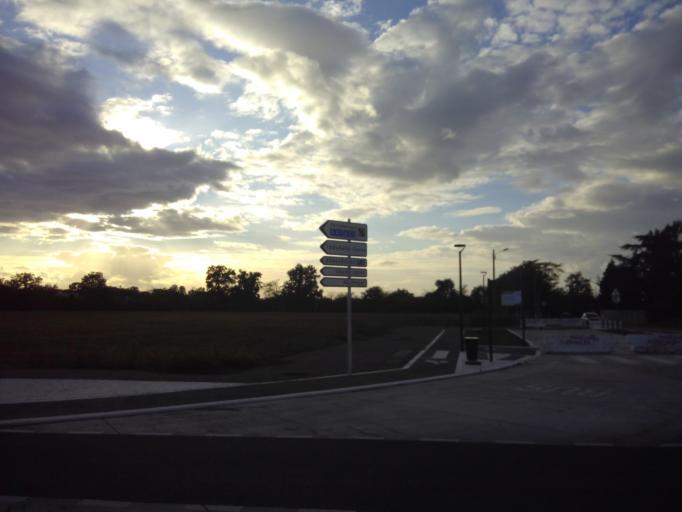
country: FR
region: Midi-Pyrenees
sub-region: Departement de la Haute-Garonne
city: Launaguet
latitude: 43.6546
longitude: 1.4592
